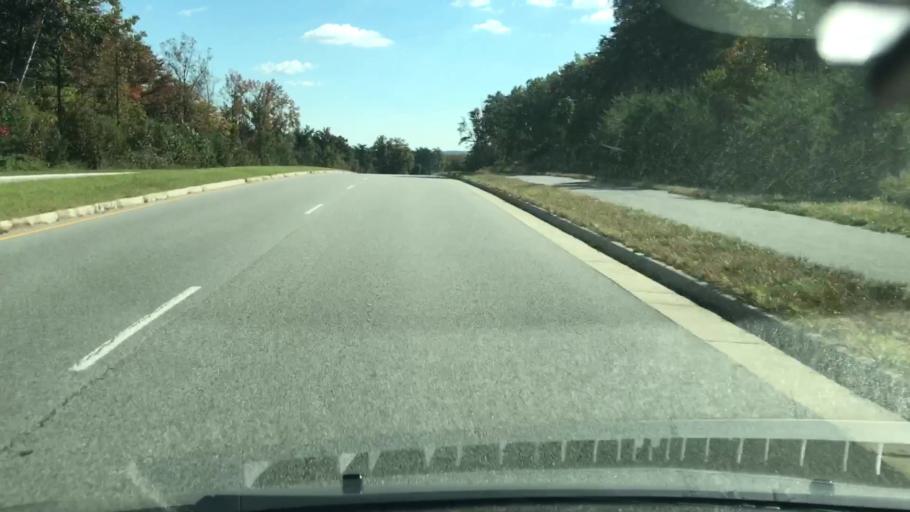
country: US
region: Virginia
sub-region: Fairfax County
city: Woodlawn
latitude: 38.7276
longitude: -77.1404
